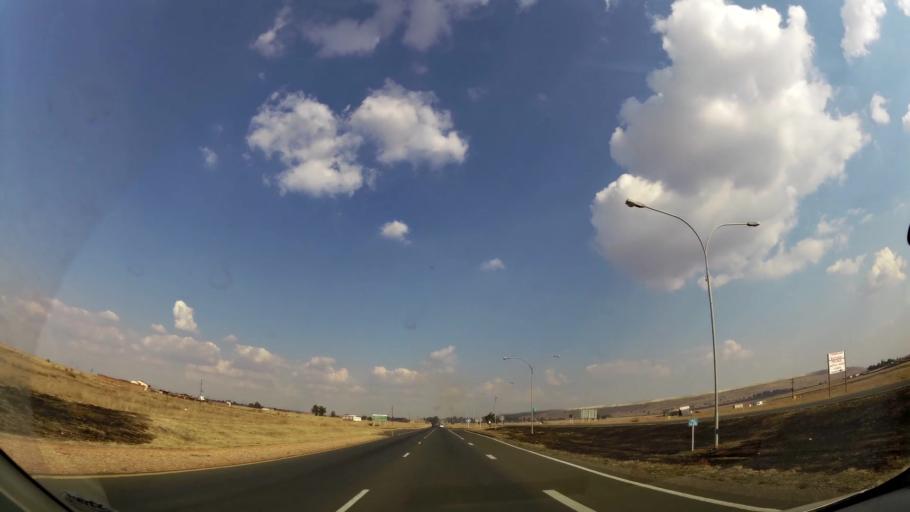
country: ZA
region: Gauteng
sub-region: Ekurhuleni Metropolitan Municipality
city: Brakpan
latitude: -26.3119
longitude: 28.3369
